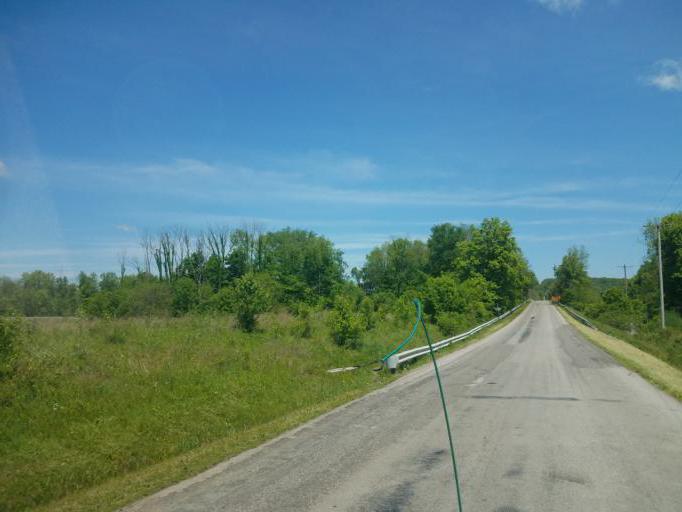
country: US
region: Ohio
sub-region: Ashland County
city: Ashland
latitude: 40.8600
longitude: -82.2501
